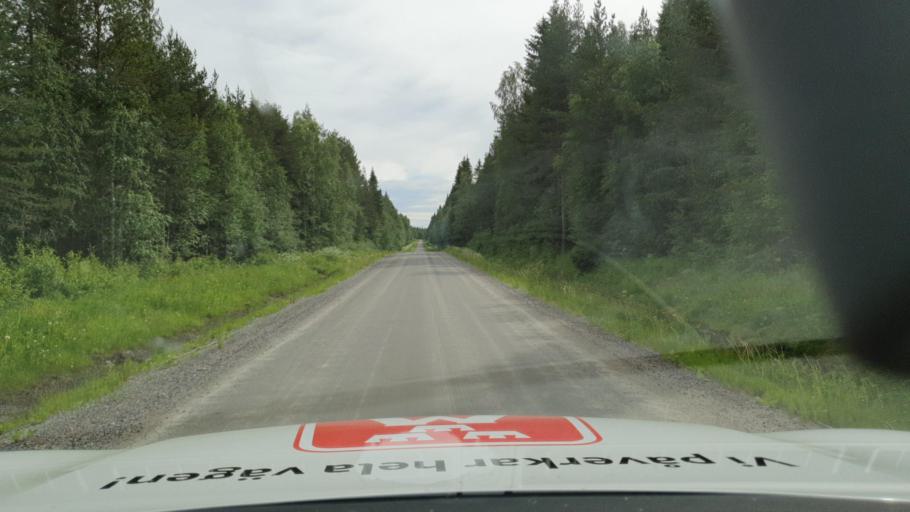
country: SE
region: Vaesterbotten
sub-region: Skelleftea Kommun
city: Burea
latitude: 64.4353
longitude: 21.0158
